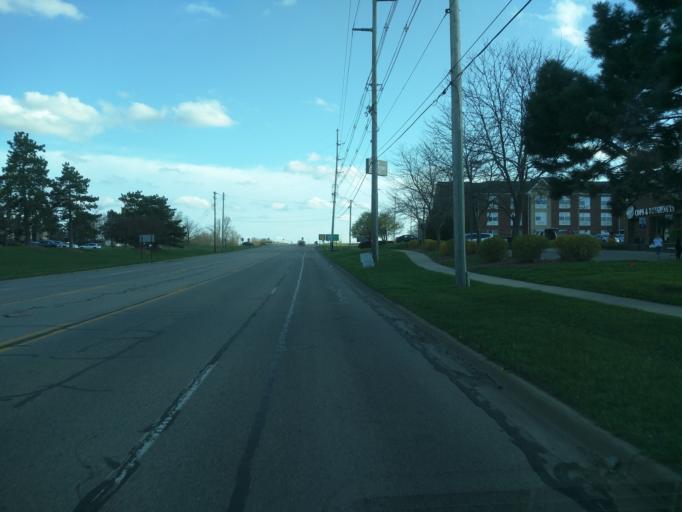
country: US
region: Michigan
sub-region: Eaton County
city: Waverly
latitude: 42.7239
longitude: -84.6424
